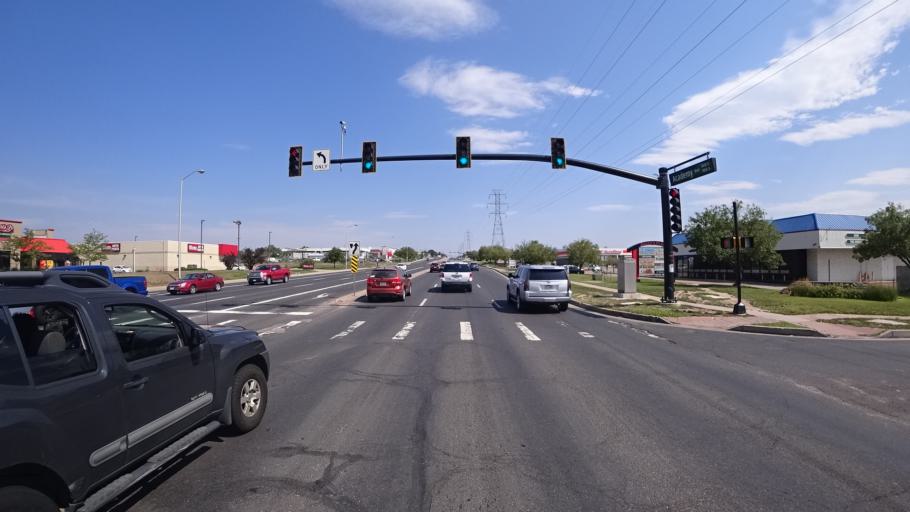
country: US
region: Colorado
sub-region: El Paso County
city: Stratmoor
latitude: 38.8050
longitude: -104.7575
